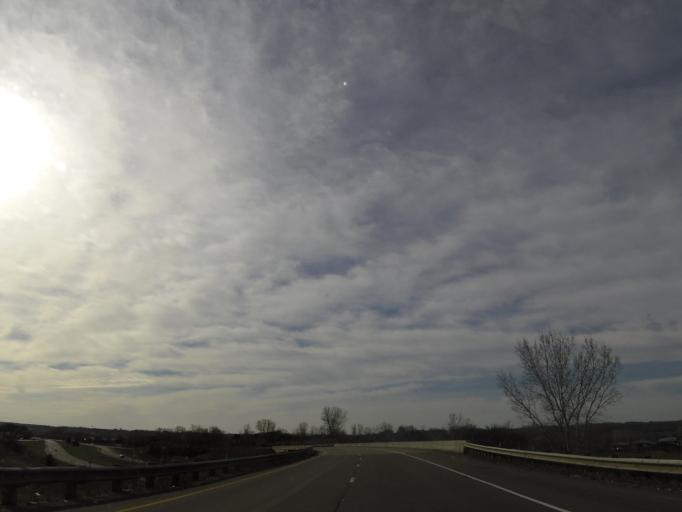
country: US
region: Minnesota
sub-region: Scott County
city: Savage
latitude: 44.7855
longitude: -93.4016
